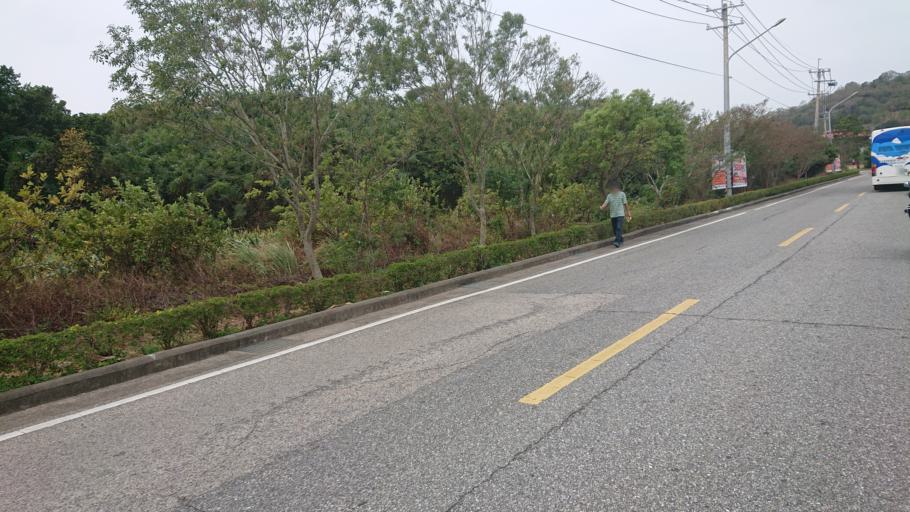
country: TW
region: Fukien
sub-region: Kinmen
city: Jincheng
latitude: 24.4270
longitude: 118.2523
